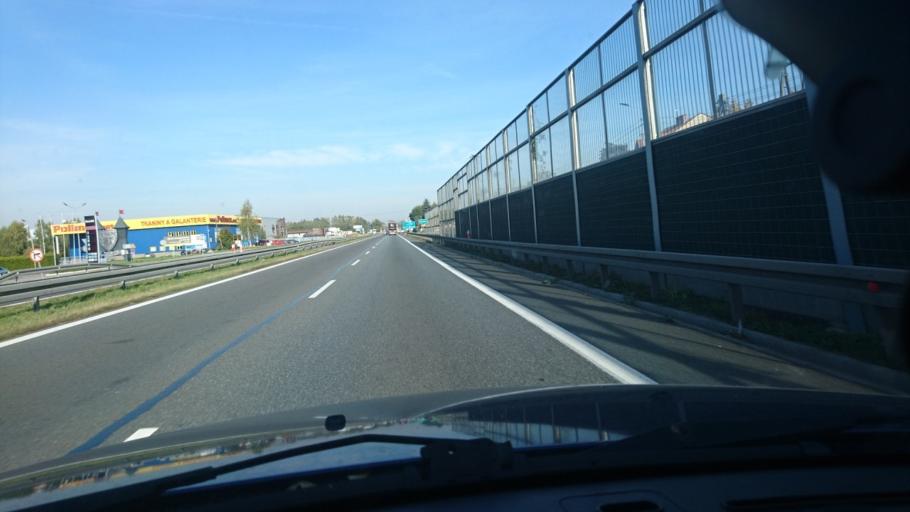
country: PL
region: Silesian Voivodeship
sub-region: Powiat pszczynski
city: Goczalkowice Zdroj
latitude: 49.9601
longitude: 18.9623
